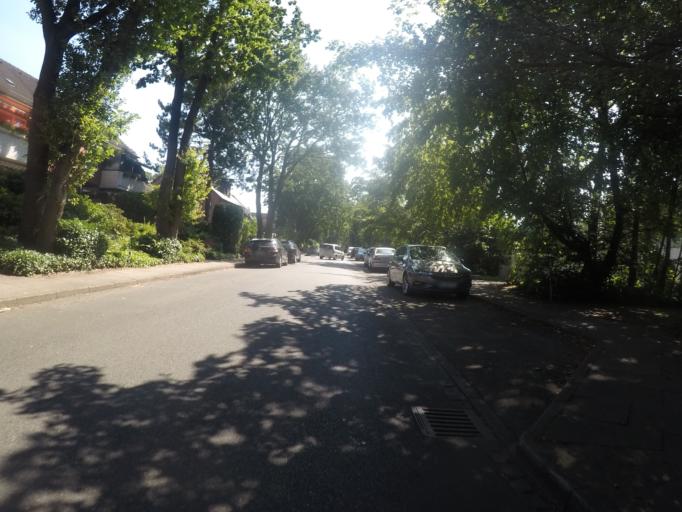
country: DE
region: Schleswig-Holstein
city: Bonningstedt
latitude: 53.6381
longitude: 9.9500
